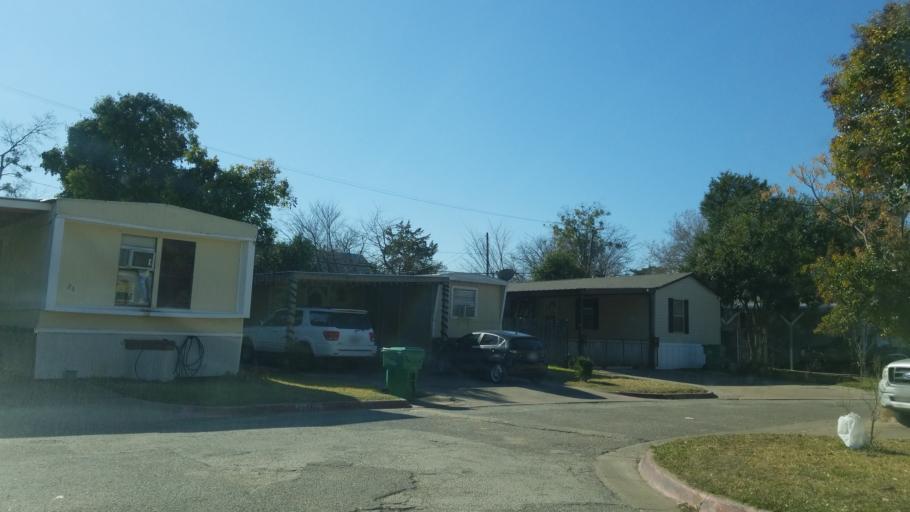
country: US
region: Texas
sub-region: Dallas County
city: Cockrell Hill
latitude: 32.7586
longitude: -96.9122
